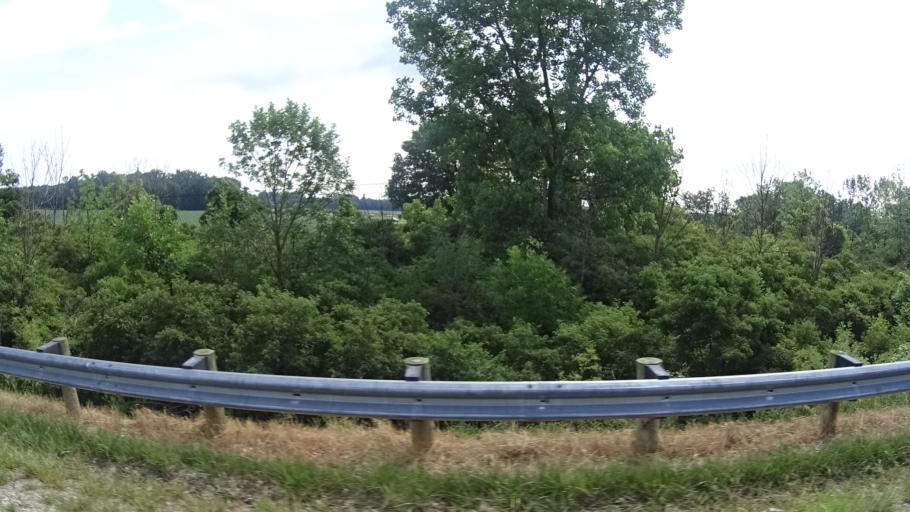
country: US
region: Ohio
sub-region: Lorain County
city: Vermilion
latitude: 41.3906
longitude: -82.4061
